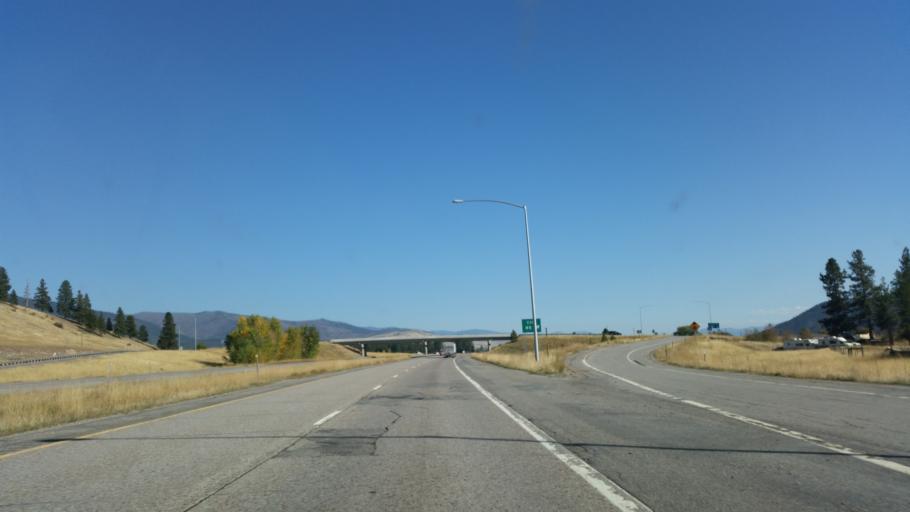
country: US
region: Montana
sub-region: Missoula County
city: Frenchtown
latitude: 47.0334
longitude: -114.3270
